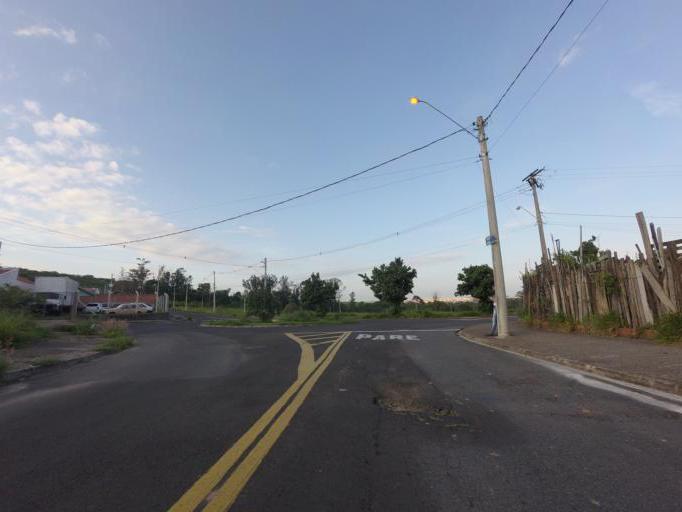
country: BR
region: Sao Paulo
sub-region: Piracicaba
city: Piracicaba
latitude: -22.7635
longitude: -47.6097
